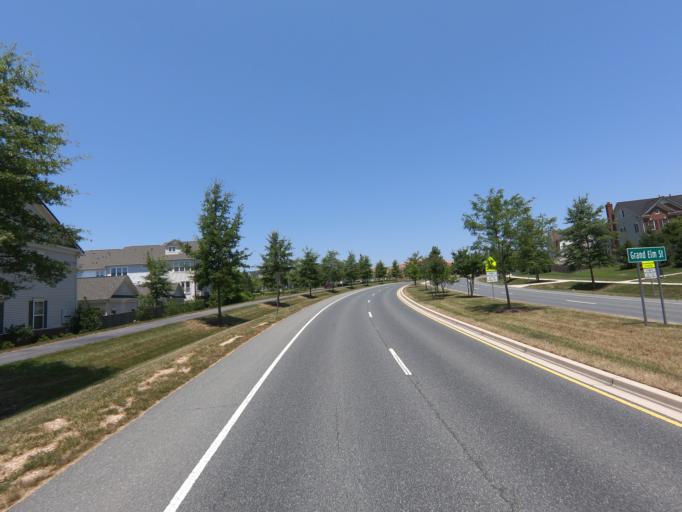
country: US
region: Maryland
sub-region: Montgomery County
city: Clarksburg
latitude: 39.2345
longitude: -77.2611
